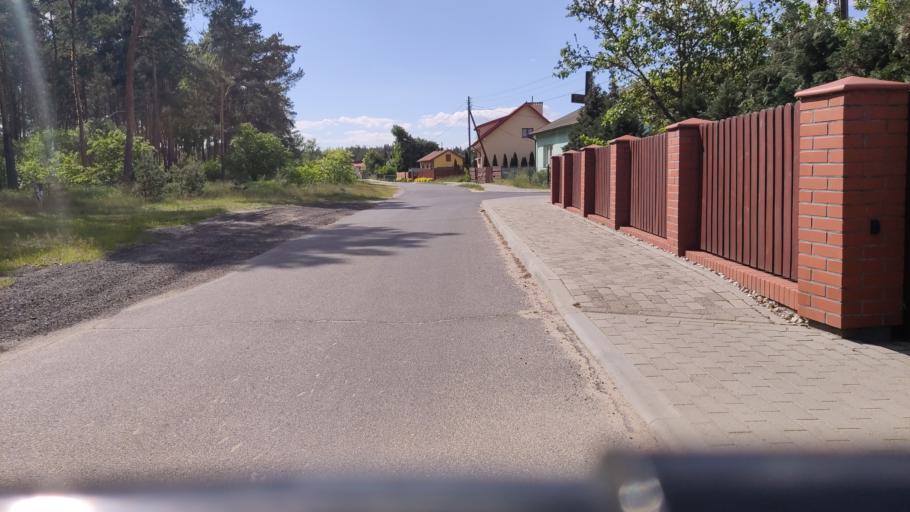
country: PL
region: Kujawsko-Pomorskie
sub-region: Wloclawek
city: Wloclawek
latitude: 52.6031
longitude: 19.0808
